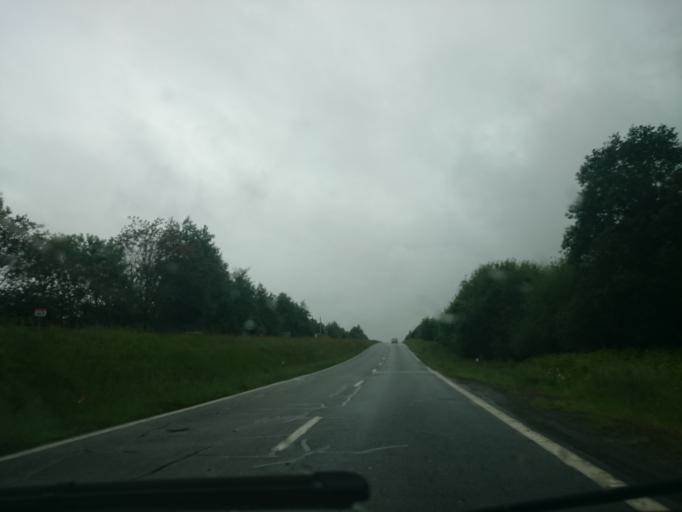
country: FR
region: Brittany
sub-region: Departement d'Ille-et-Vilaine
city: Breal-sous-Montfort
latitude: 48.0646
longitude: -1.8637
